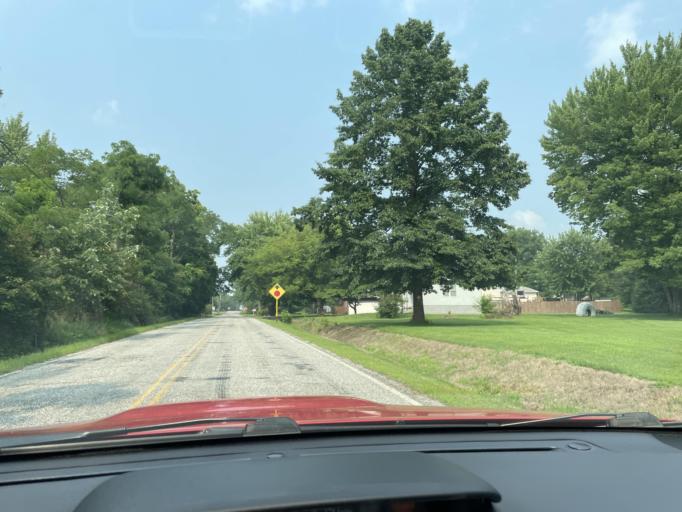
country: US
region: Ohio
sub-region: Trumbull County
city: McDonald
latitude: 41.1631
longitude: -80.7381
